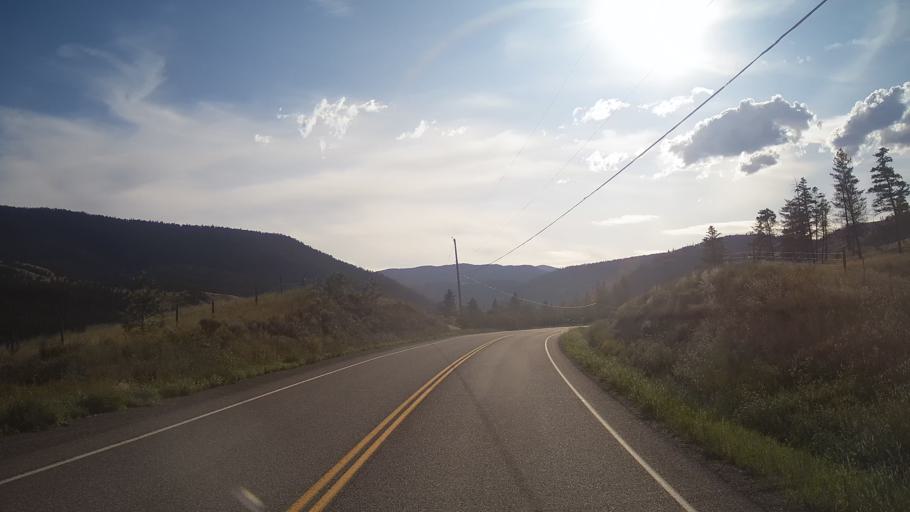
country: CA
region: British Columbia
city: Cache Creek
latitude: 50.8869
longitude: -121.4574
